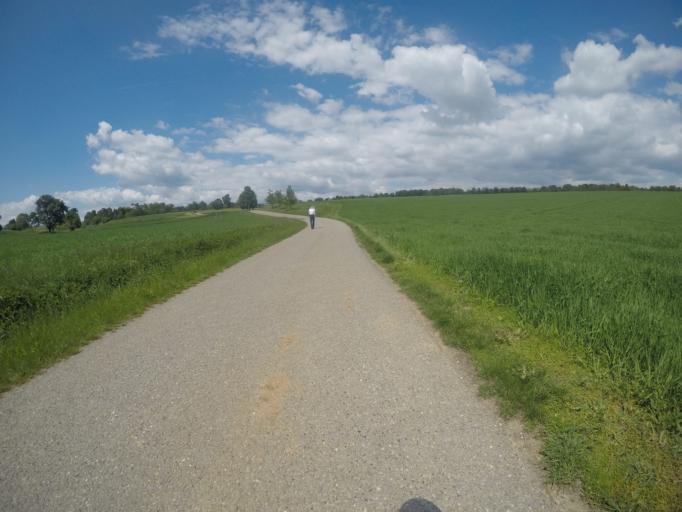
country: DE
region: Baden-Wuerttemberg
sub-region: Regierungsbezirk Stuttgart
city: Herrenberg
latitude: 48.5845
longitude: 8.8263
